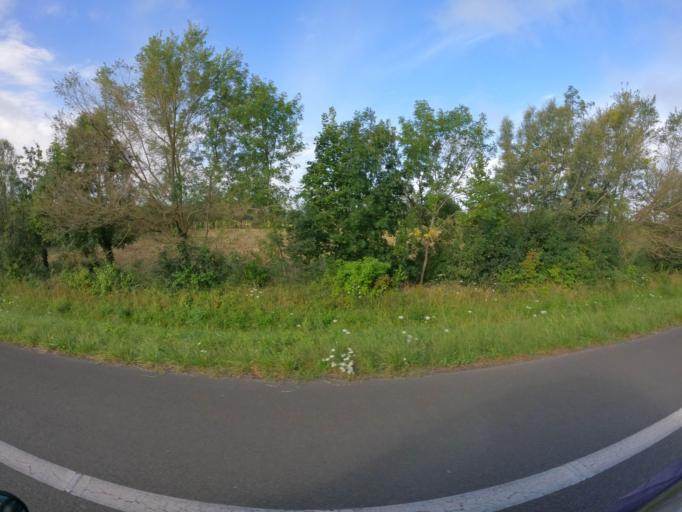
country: FR
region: Pays de la Loire
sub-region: Departement de Maine-et-Loire
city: Vivy
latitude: 47.2977
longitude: -0.0280
